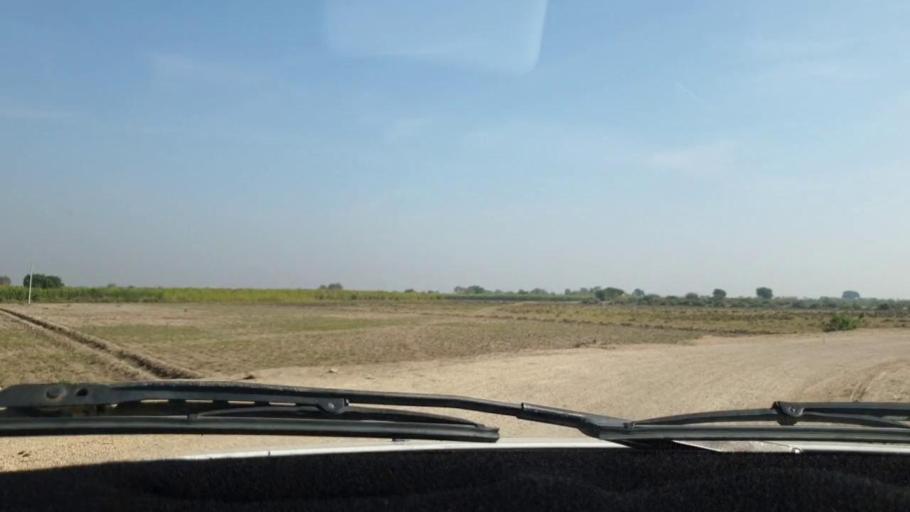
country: PK
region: Sindh
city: Tando Muhammad Khan
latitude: 24.9906
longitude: 68.4683
